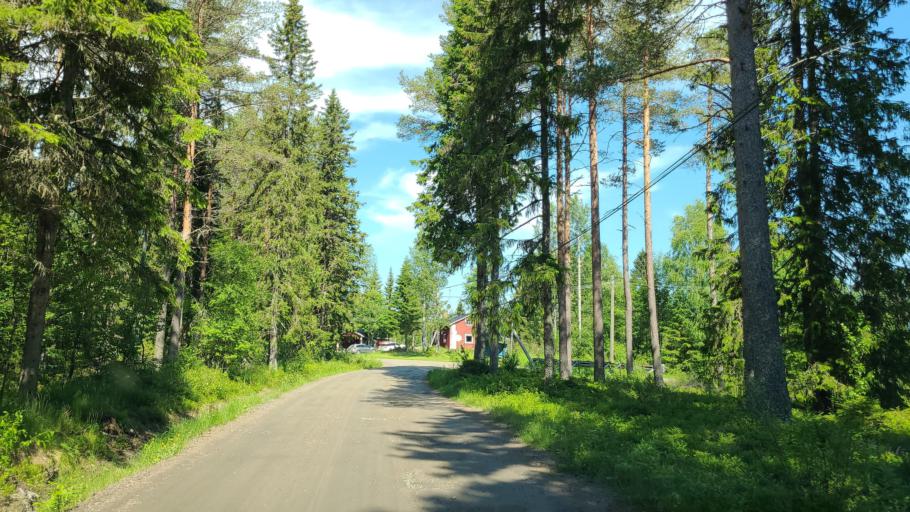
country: SE
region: Vaesterbotten
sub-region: Robertsfors Kommun
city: Robertsfors
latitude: 64.1438
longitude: 20.9609
